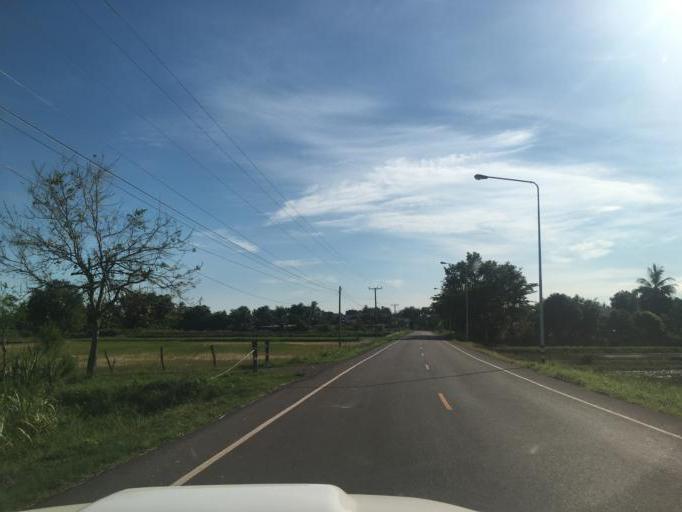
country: TH
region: Changwat Udon Thani
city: Kut Chap
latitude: 17.5155
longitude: 102.5932
